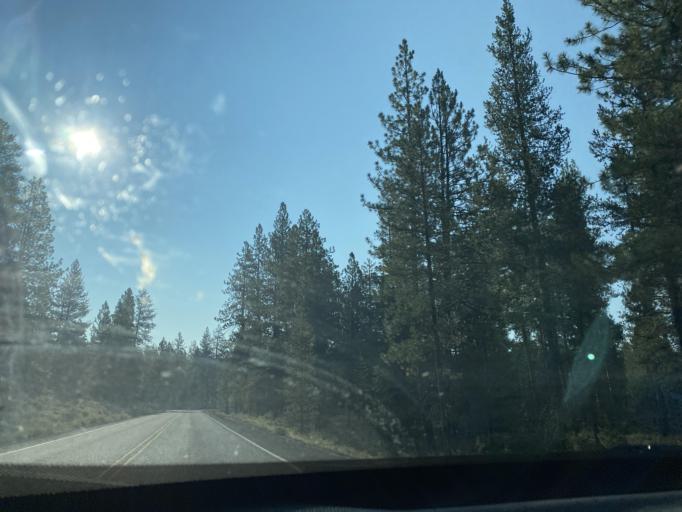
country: US
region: Oregon
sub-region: Deschutes County
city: La Pine
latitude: 43.7065
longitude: -121.3989
